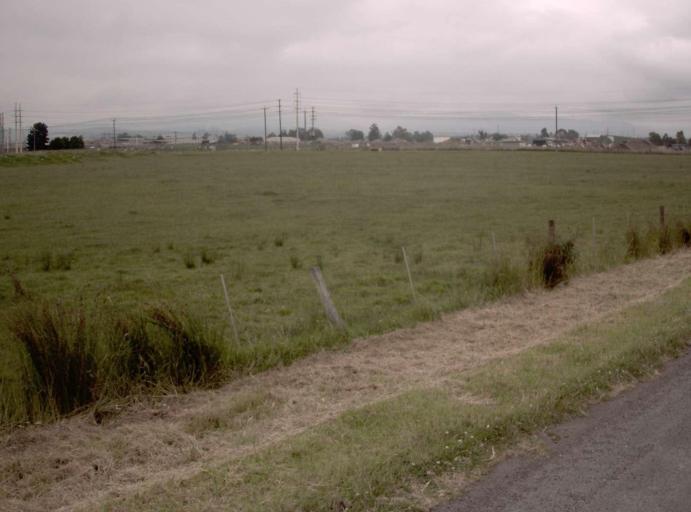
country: AU
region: Victoria
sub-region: Latrobe
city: Morwell
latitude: -38.2519
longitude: 146.4257
